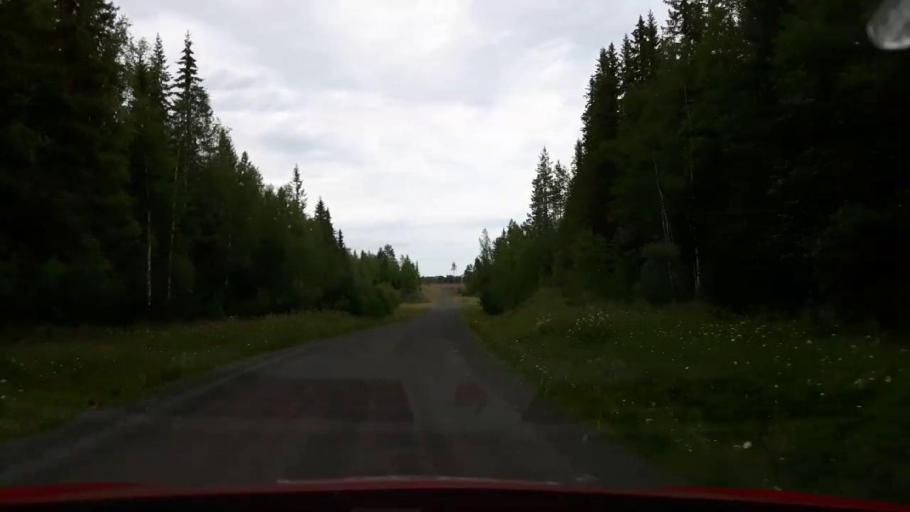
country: SE
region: Jaemtland
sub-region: OEstersunds Kommun
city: Lit
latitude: 63.4086
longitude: 15.2389
